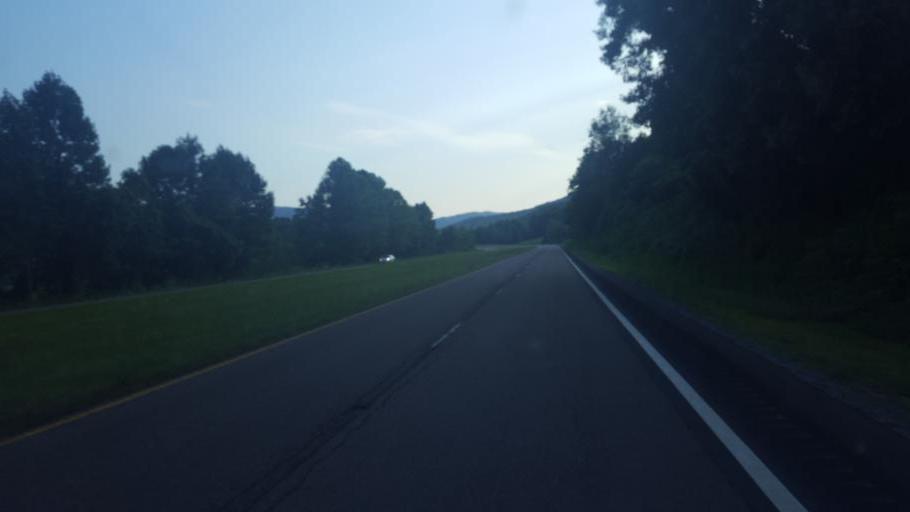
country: US
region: Virginia
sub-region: Wise County
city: Big Stone Gap
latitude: 36.7951
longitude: -82.8069
